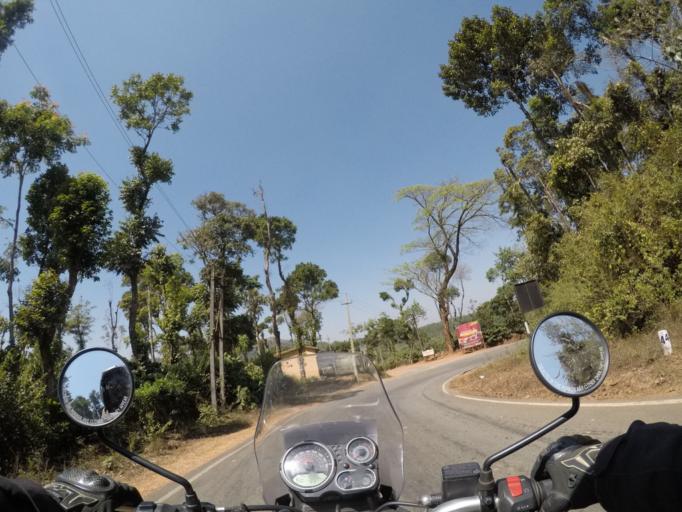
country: IN
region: Karnataka
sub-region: Chikmagalur
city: Mudigere
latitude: 13.0336
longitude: 75.6873
